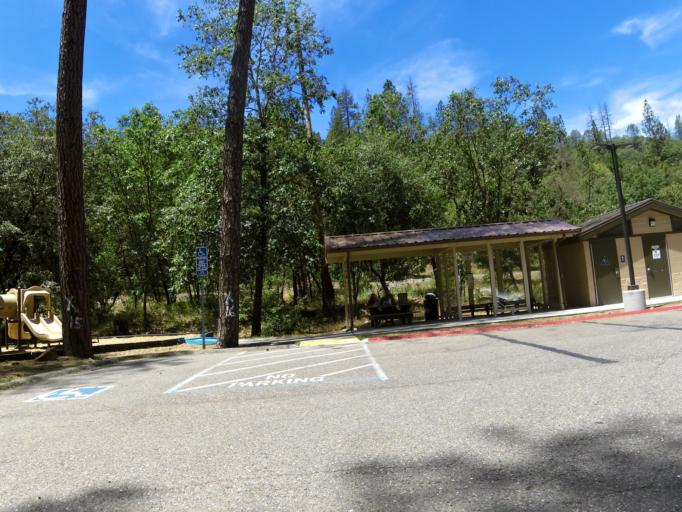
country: US
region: California
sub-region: Mariposa County
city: Midpines
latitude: 37.5464
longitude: -119.9199
